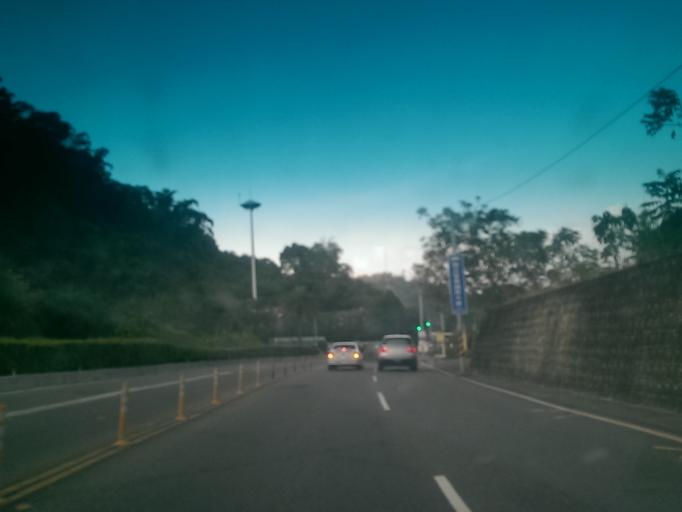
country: TW
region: Taiwan
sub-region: Nantou
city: Puli
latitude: 23.9482
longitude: 120.9374
